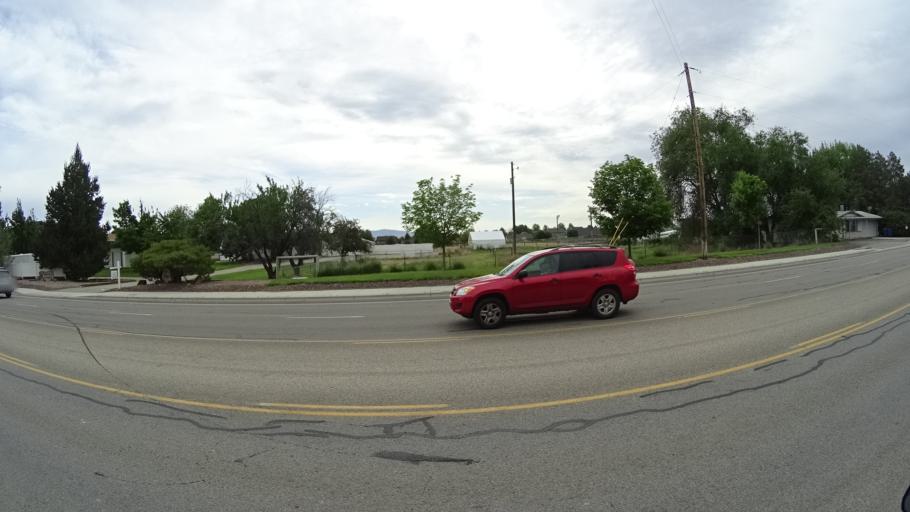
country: US
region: Idaho
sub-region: Ada County
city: Meridian
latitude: 43.5789
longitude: -116.3544
